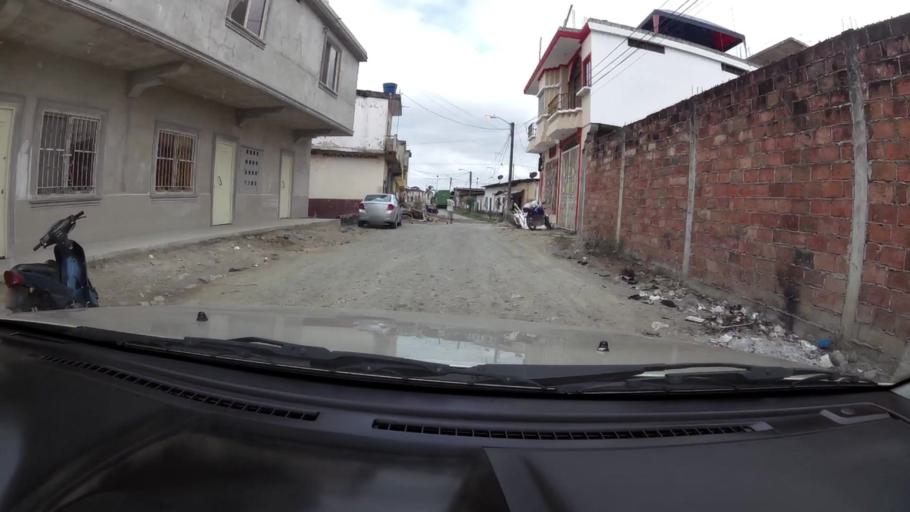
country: EC
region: Guayas
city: Naranjal
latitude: -2.6783
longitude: -79.6175
